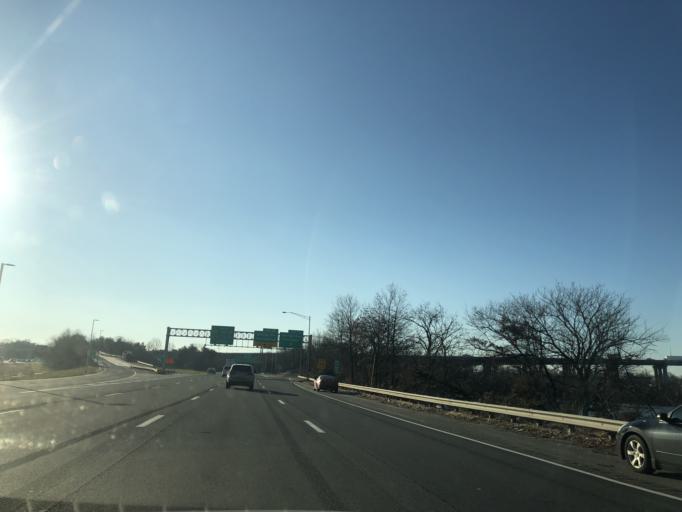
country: US
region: New Jersey
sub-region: Camden County
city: Gloucester City
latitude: 39.9061
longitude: -75.1140
